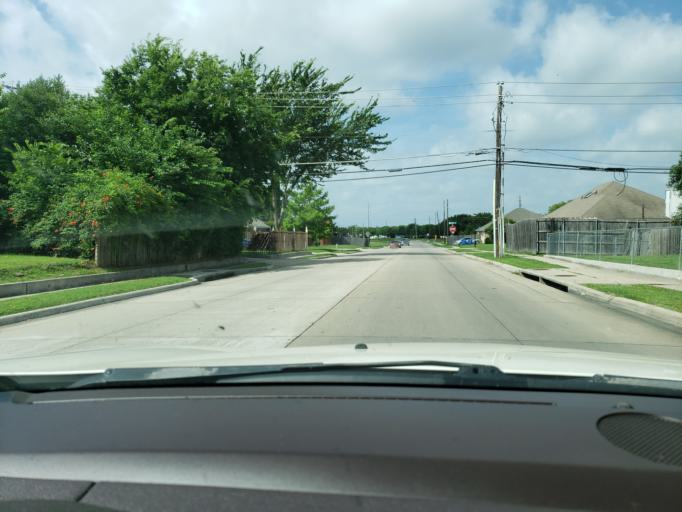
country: US
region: Texas
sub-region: Dallas County
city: Rowlett
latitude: 32.9116
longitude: -96.5738
